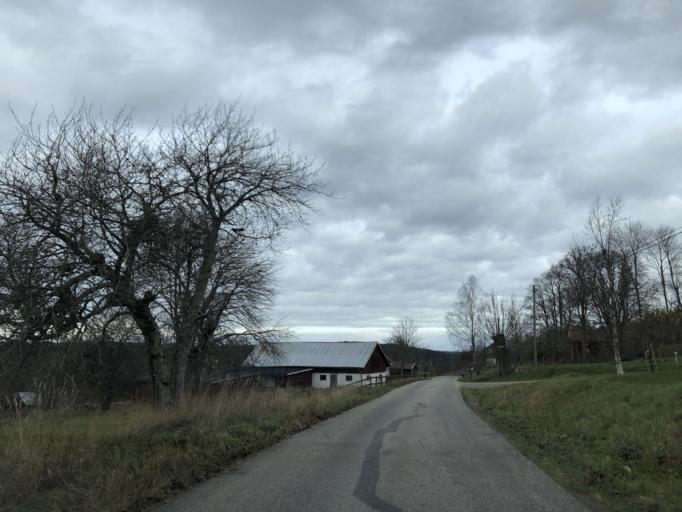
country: SE
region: Vaestra Goetaland
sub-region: Ulricehamns Kommun
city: Ulricehamn
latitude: 57.7204
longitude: 13.3590
